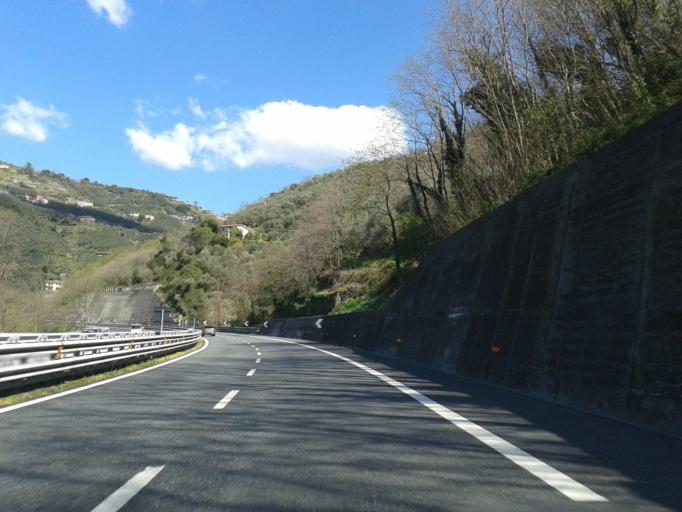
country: IT
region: Liguria
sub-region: Provincia di Genova
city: Cogorno
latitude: 44.2994
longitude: 9.3842
